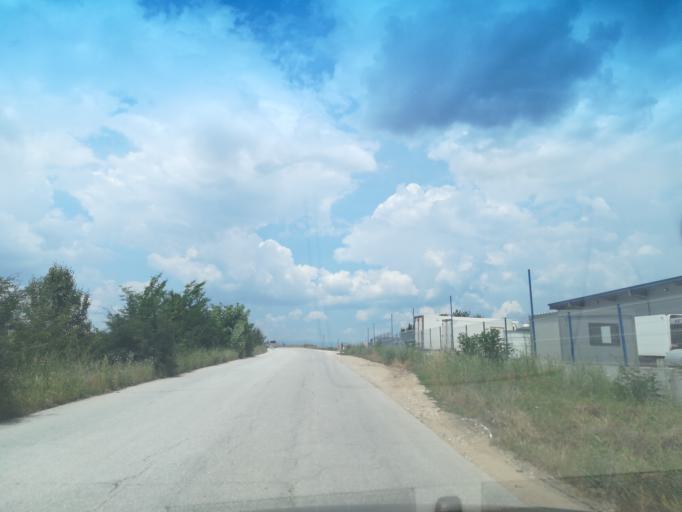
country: BG
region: Stara Zagora
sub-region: Obshtina Chirpan
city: Chirpan
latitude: 42.1801
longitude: 25.2070
